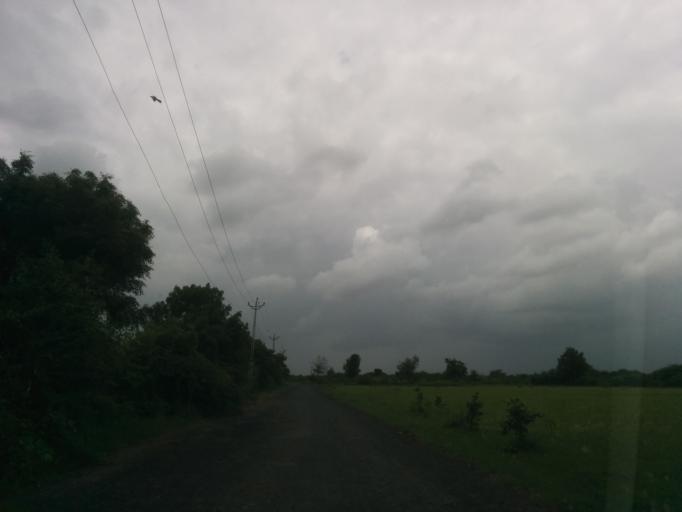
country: IN
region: Gujarat
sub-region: Ahmadabad
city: Sanand
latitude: 23.0683
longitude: 72.3886
